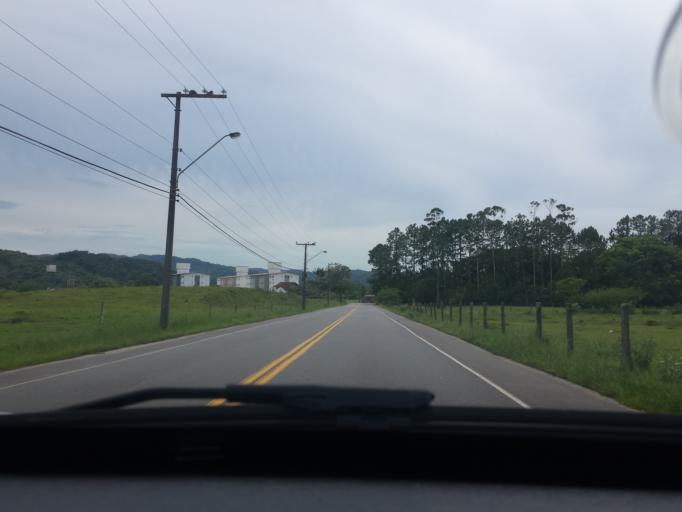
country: BR
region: Santa Catarina
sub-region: Blumenau
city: Blumenau
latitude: -26.9050
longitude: -49.0223
